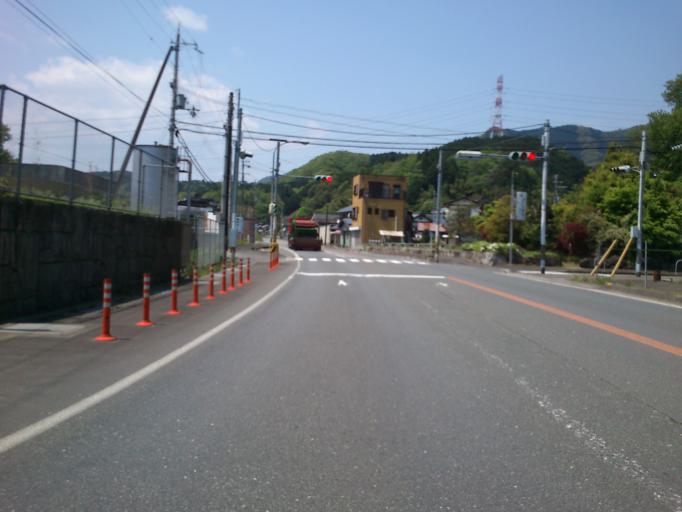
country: JP
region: Kyoto
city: Fukuchiyama
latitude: 35.3248
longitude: 135.0431
